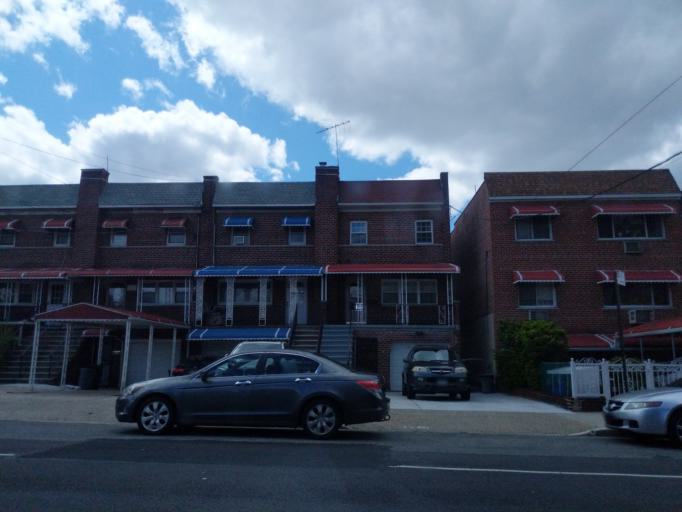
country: US
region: New York
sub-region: Bronx
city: The Bronx
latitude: 40.8689
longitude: -73.8615
